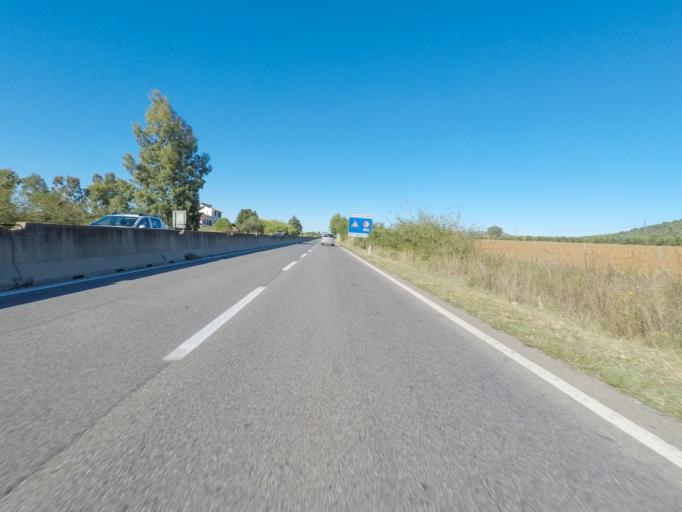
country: IT
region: Tuscany
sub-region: Provincia di Grosseto
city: Grosseto
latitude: 42.6957
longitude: 11.1379
